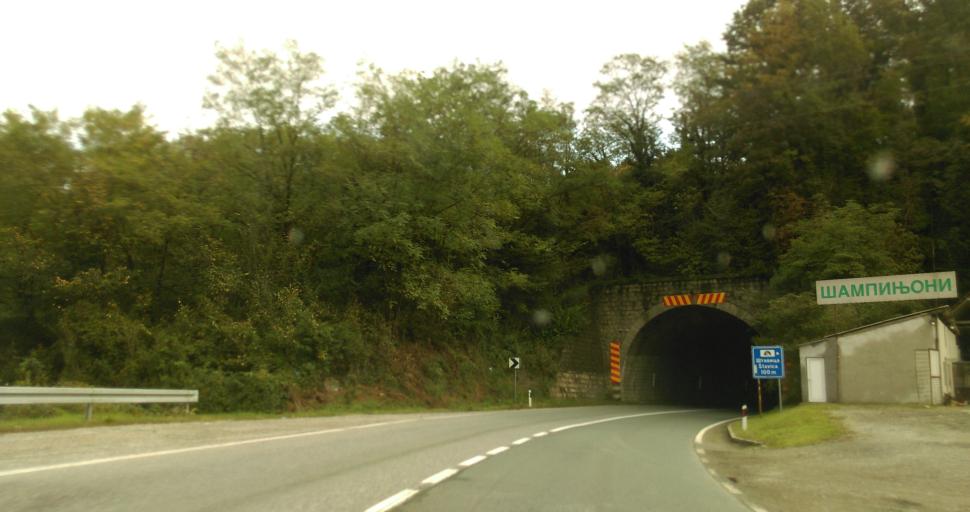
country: RS
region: Central Serbia
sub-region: Kolubarski Okrug
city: Ljig
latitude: 44.1910
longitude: 20.3188
